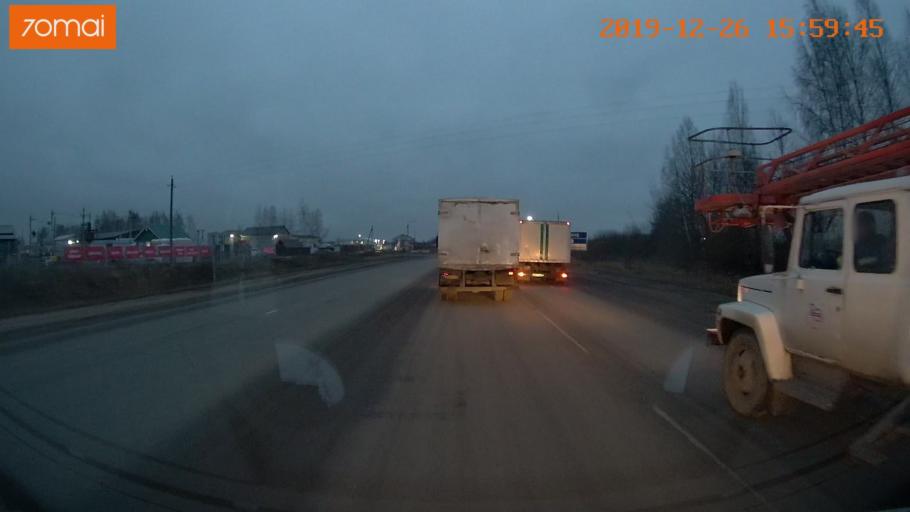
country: RU
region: Jaroslavl
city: Rybinsk
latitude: 58.0296
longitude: 38.8045
